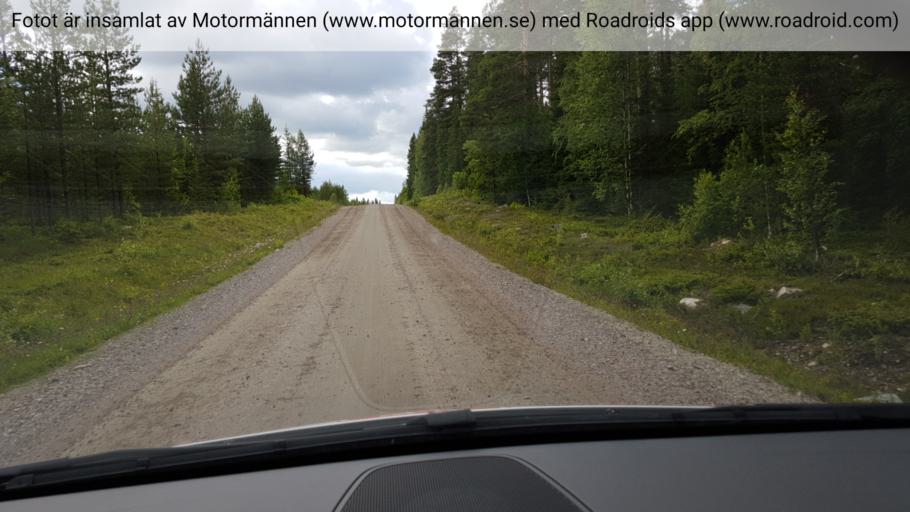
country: SE
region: Vaesterbotten
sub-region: Dorotea Kommun
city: Dorotea
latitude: 63.9193
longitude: 16.2059
